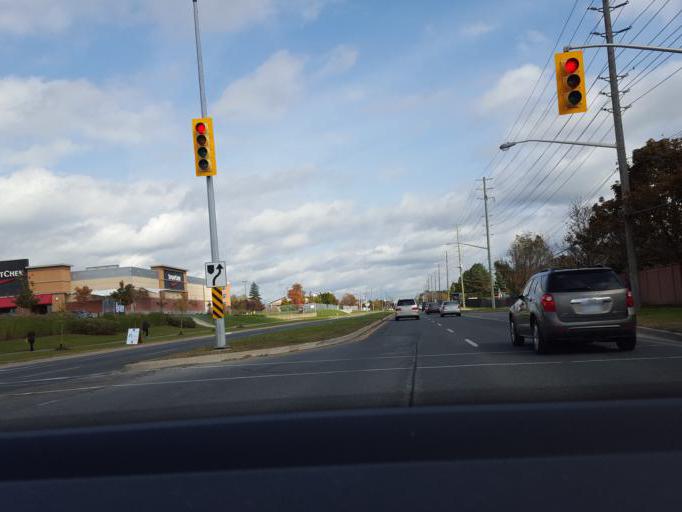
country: CA
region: Ontario
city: Oshawa
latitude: 43.9182
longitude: -78.9446
